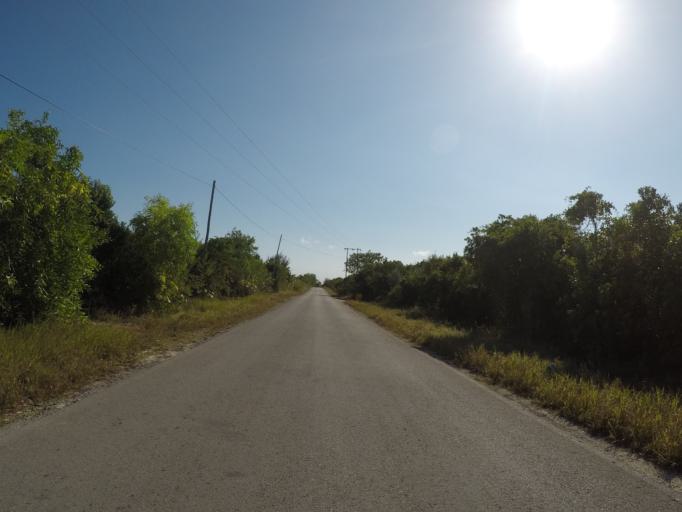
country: TZ
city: Kiwengwa
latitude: -6.1432
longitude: 39.5075
